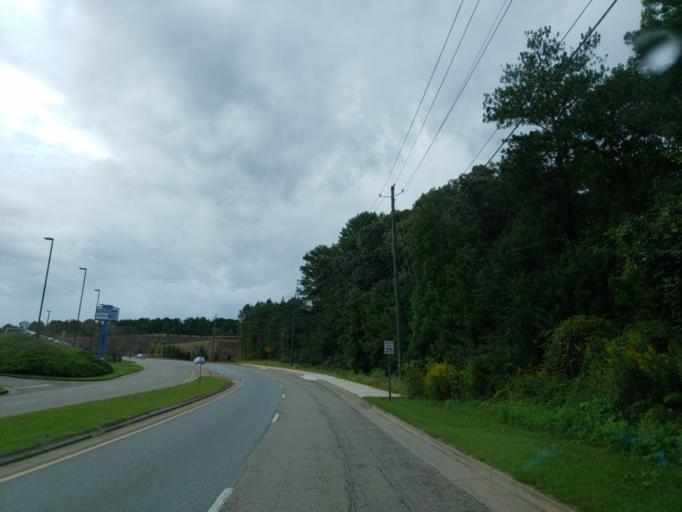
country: US
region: Georgia
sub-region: Cherokee County
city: Woodstock
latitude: 34.1047
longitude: -84.5280
